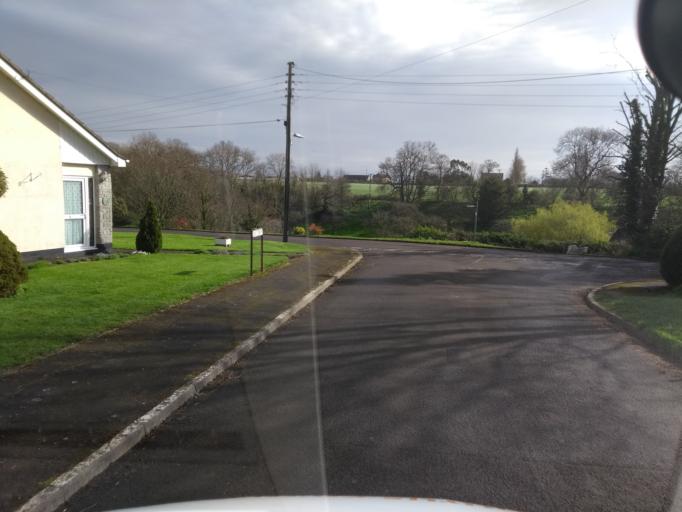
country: GB
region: England
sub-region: Somerset
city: Woolavington
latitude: 51.1616
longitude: -2.9203
